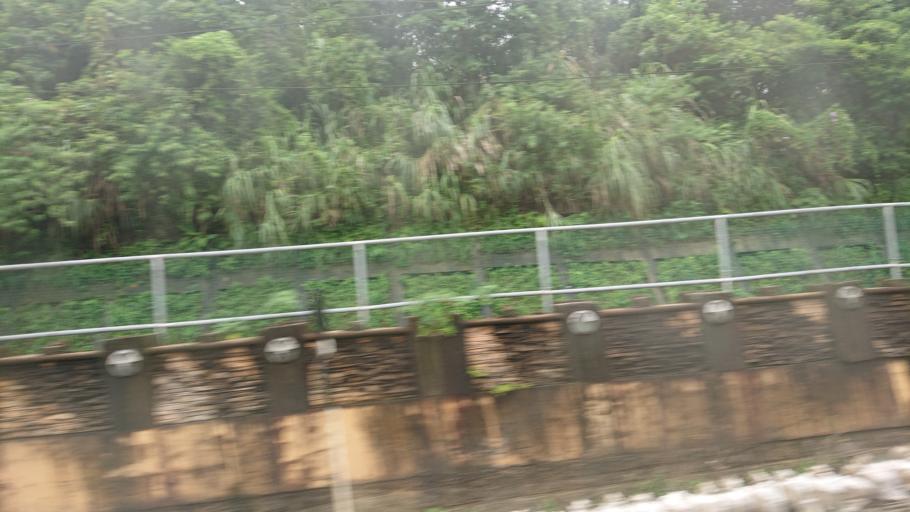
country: TW
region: Taiwan
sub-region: Keelung
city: Keelung
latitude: 25.0820
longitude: 121.7035
